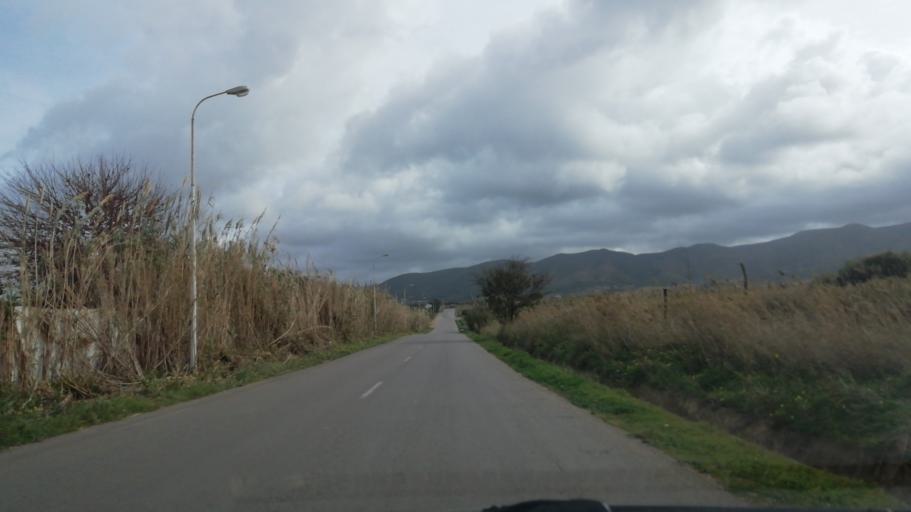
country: DZ
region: Oran
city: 'Ain el Turk
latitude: 35.7007
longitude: -0.8882
